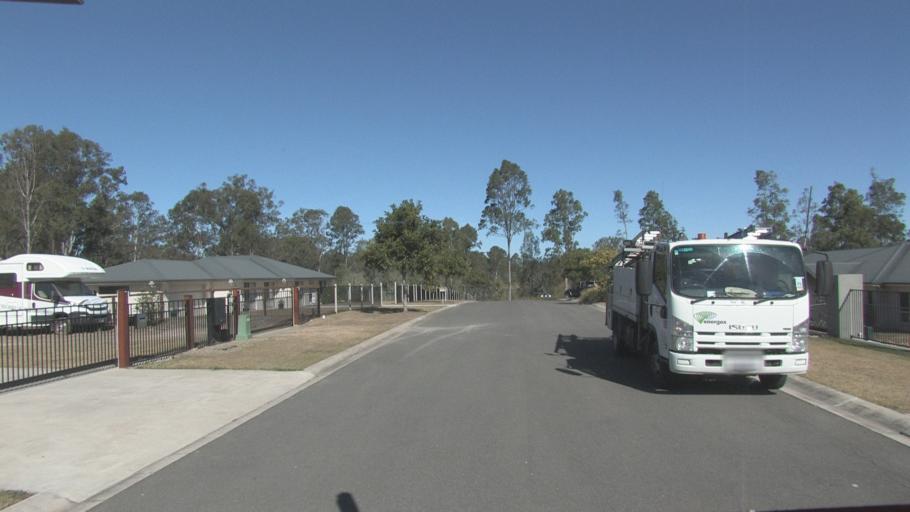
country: AU
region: Queensland
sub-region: Logan
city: North Maclean
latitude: -27.8289
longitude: 152.9850
